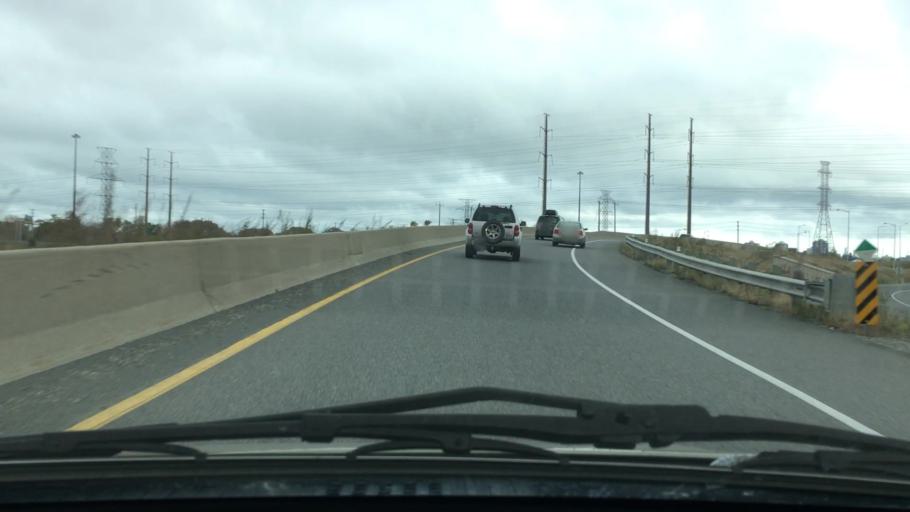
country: CA
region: Ontario
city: Burlington
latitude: 43.3347
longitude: -79.8322
